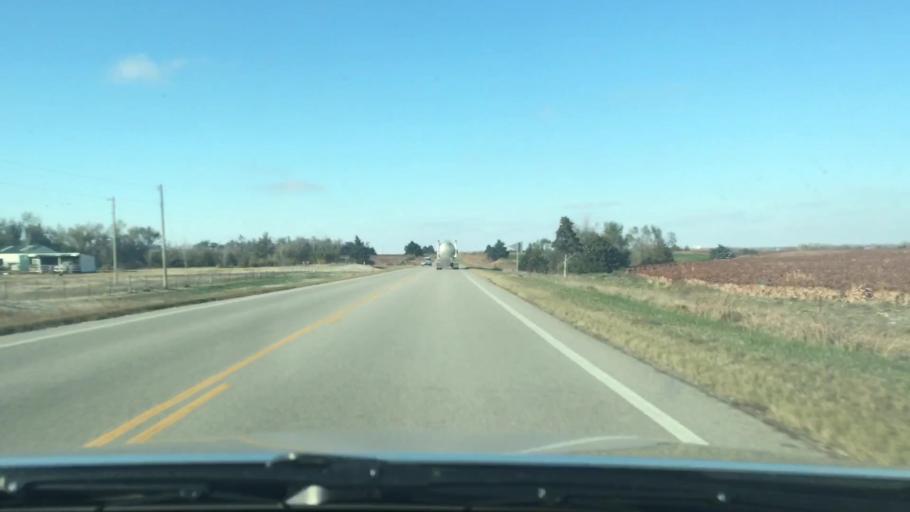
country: US
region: Kansas
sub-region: Rice County
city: Sterling
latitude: 38.1475
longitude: -98.2033
